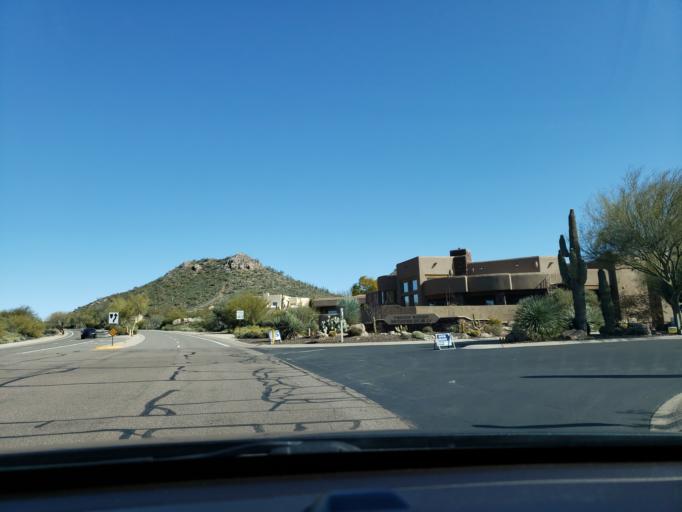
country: US
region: Arizona
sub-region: Maricopa County
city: Carefree
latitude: 33.7045
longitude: -111.8390
